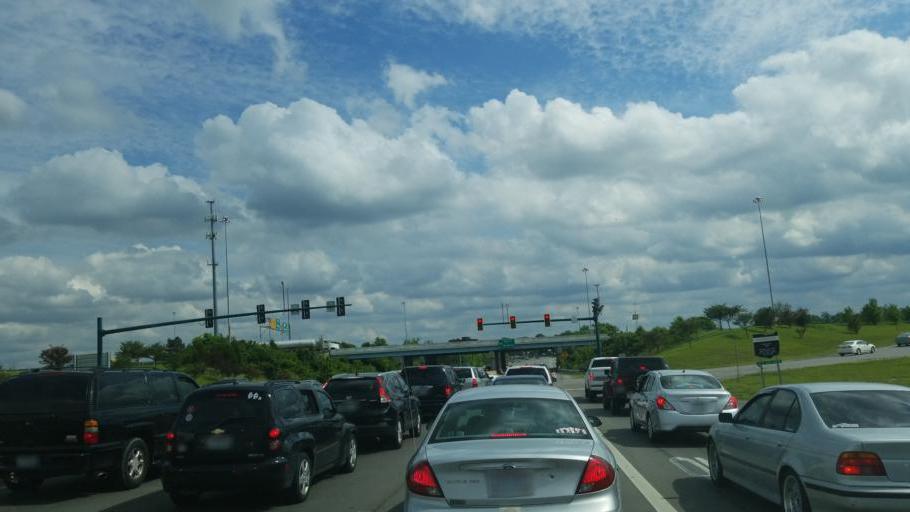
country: US
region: Ohio
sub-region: Franklin County
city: Reynoldsburg
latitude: 39.9350
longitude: -82.7897
